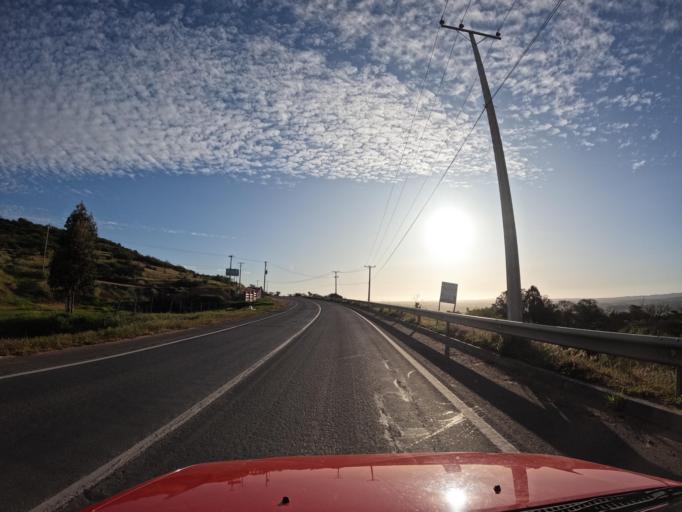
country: CL
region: Valparaiso
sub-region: San Antonio Province
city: San Antonio
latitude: -34.0888
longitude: -71.6814
